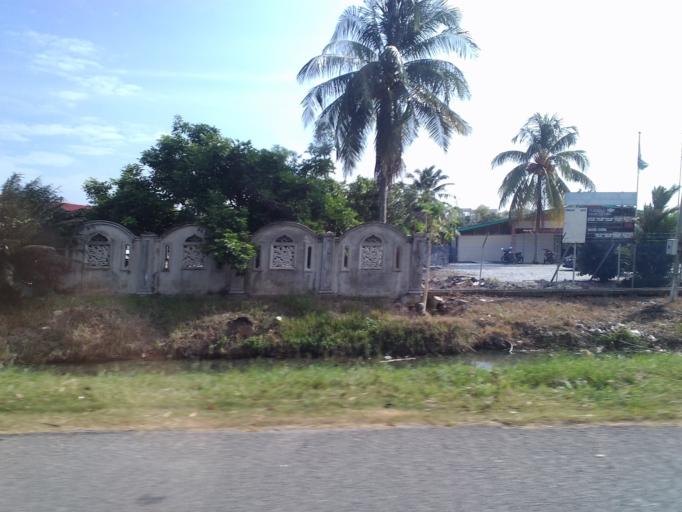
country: MY
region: Kedah
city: Gurun
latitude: 5.9551
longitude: 100.4071
